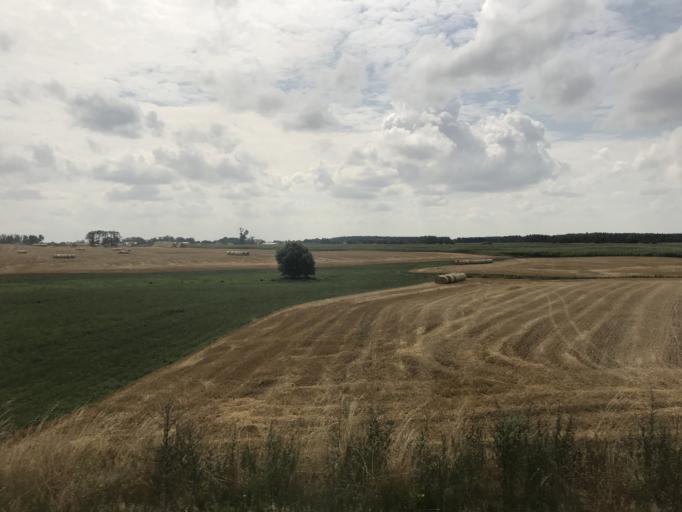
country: PL
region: Greater Poland Voivodeship
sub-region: Powiat gnieznienski
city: Gniezno
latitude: 52.5131
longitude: 17.5234
